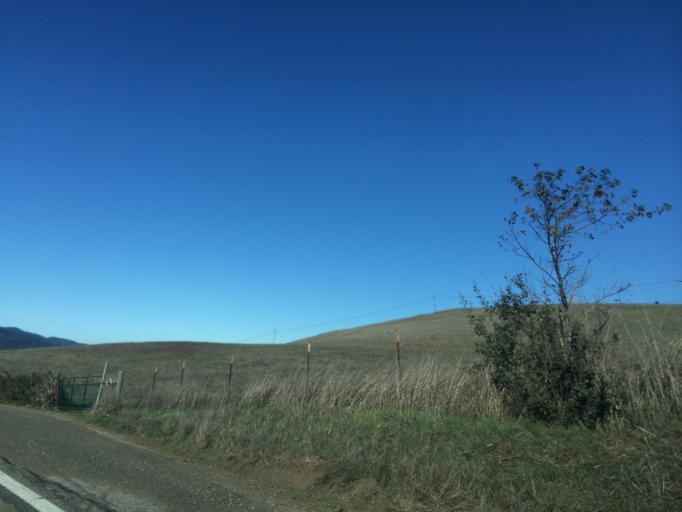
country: US
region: California
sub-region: Marin County
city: Lagunitas-Forest Knolls
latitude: 38.0466
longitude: -122.7721
